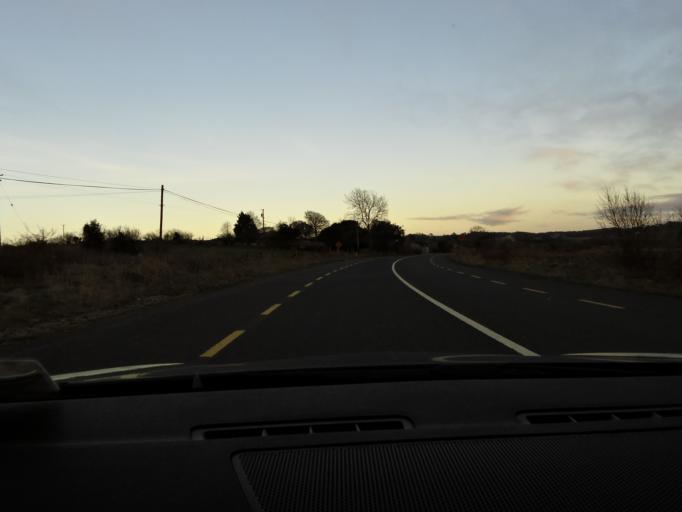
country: IE
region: Connaught
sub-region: Sligo
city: Ballymote
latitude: 53.9794
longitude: -8.4600
